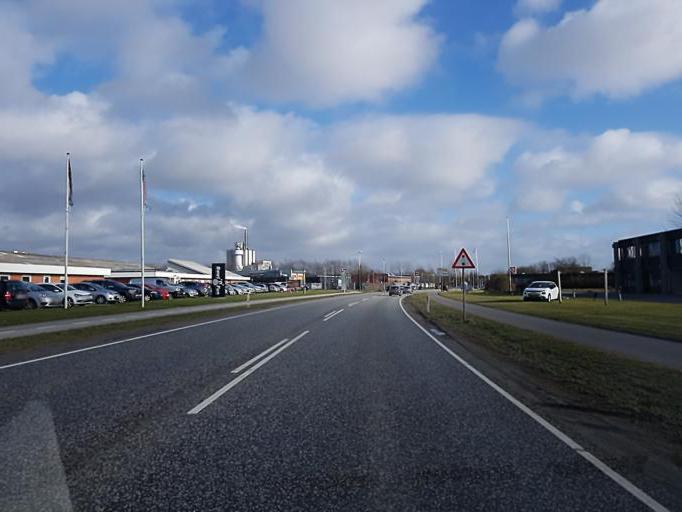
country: DK
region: Central Jutland
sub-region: Holstebro Kommune
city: Holstebro
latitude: 56.3679
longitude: 8.6367
